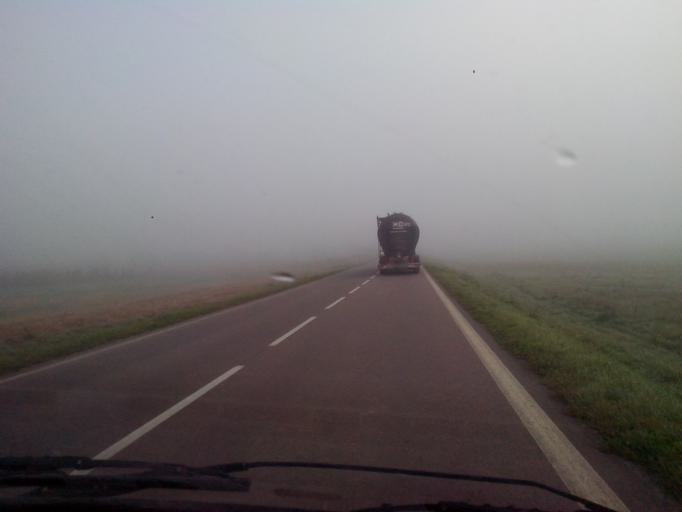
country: PL
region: Subcarpathian Voivodeship
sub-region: Powiat przemyski
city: Krasiczyn
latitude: 49.7932
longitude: 22.6362
